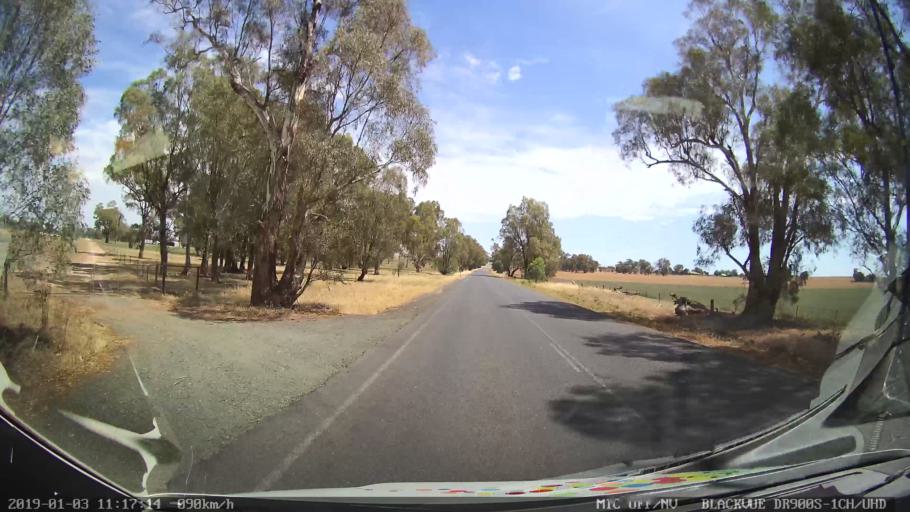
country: AU
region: New South Wales
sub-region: Young
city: Young
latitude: -34.1414
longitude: 148.2669
